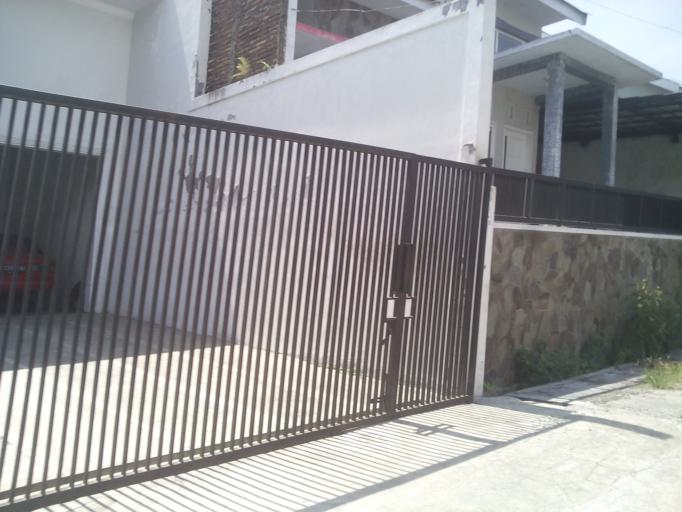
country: ID
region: East Java
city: Sumbersari Wetan
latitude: -8.1756
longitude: 113.7205
